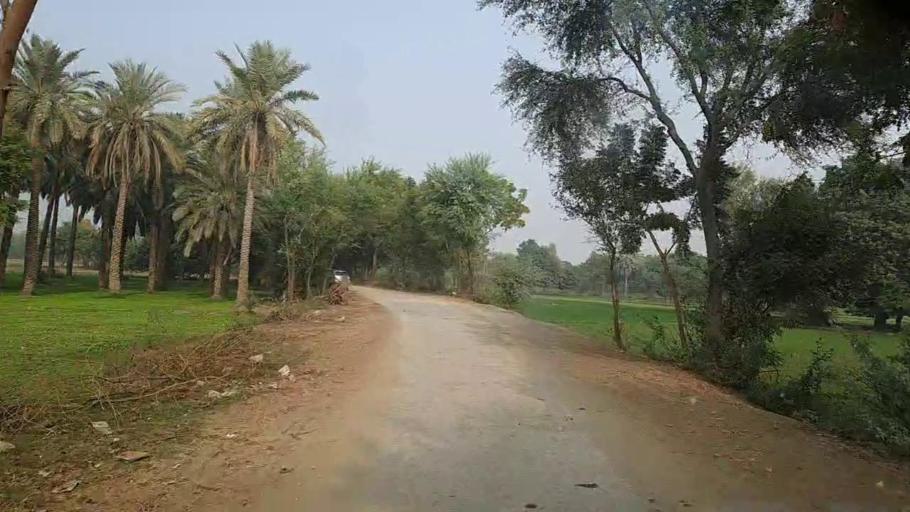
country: PK
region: Sindh
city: Bozdar
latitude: 27.1345
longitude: 68.6603
